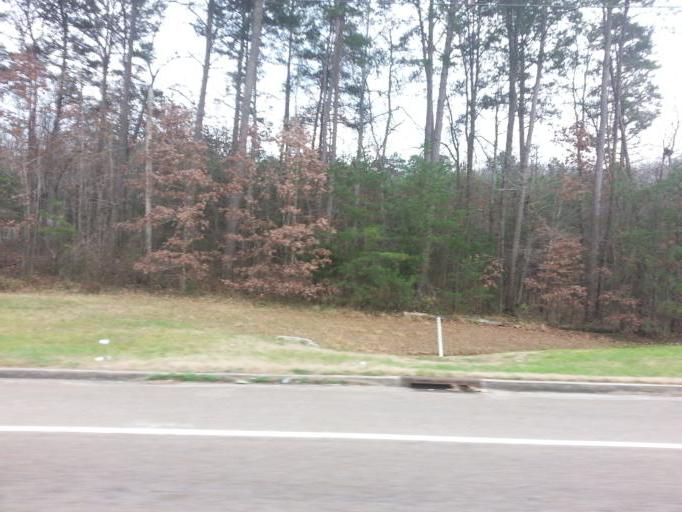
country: US
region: Tennessee
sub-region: Rhea County
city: Dayton
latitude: 35.4645
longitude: -85.0414
